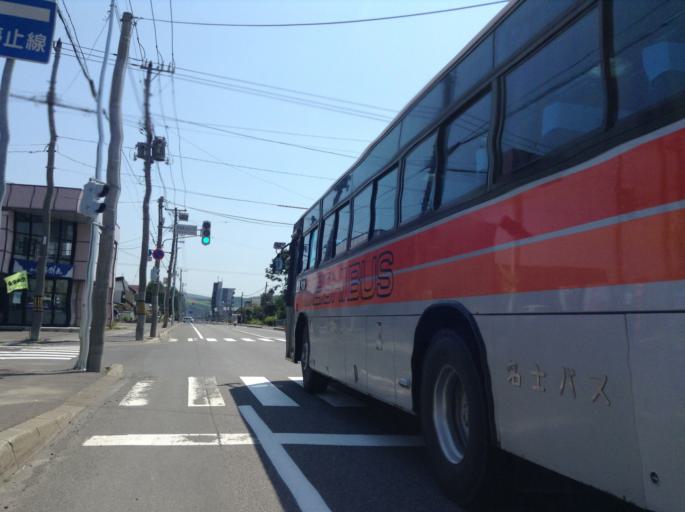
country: JP
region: Hokkaido
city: Nayoro
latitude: 44.3615
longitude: 142.4498
